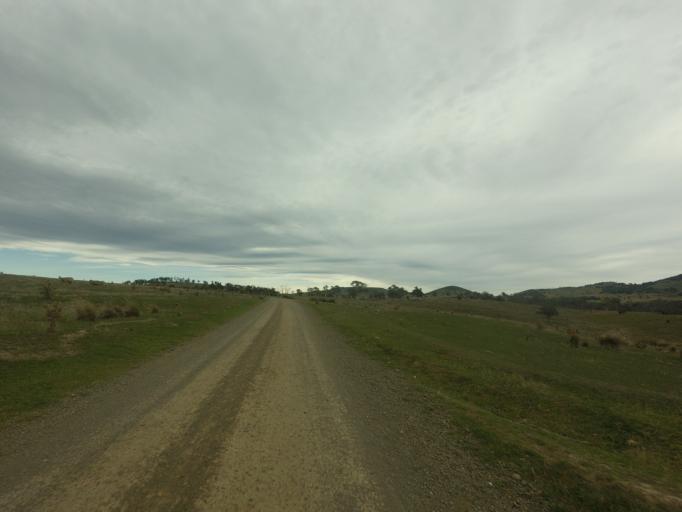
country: AU
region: Tasmania
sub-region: Derwent Valley
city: New Norfolk
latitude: -42.3921
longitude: 146.8940
